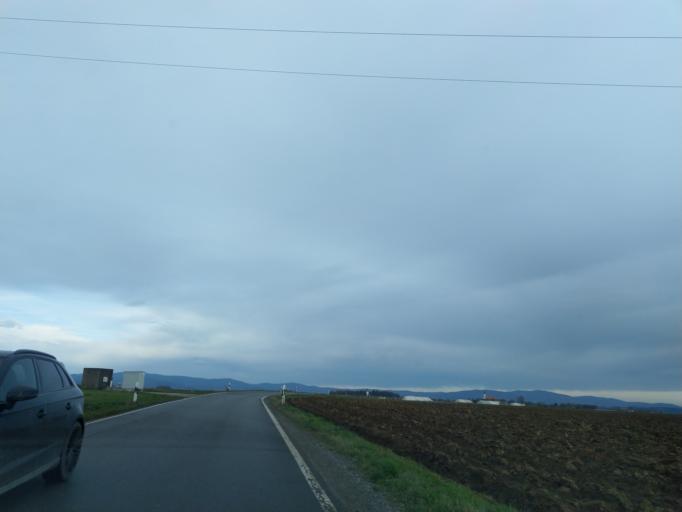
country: DE
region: Bavaria
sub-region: Lower Bavaria
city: Osterhofen
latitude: 48.6763
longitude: 12.9955
